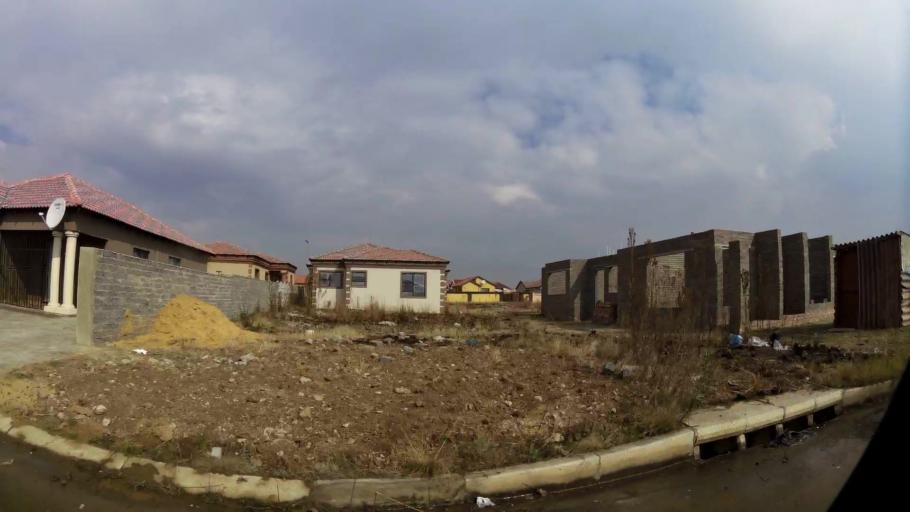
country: ZA
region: Gauteng
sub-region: Sedibeng District Municipality
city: Vanderbijlpark
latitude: -26.6820
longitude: 27.8468
